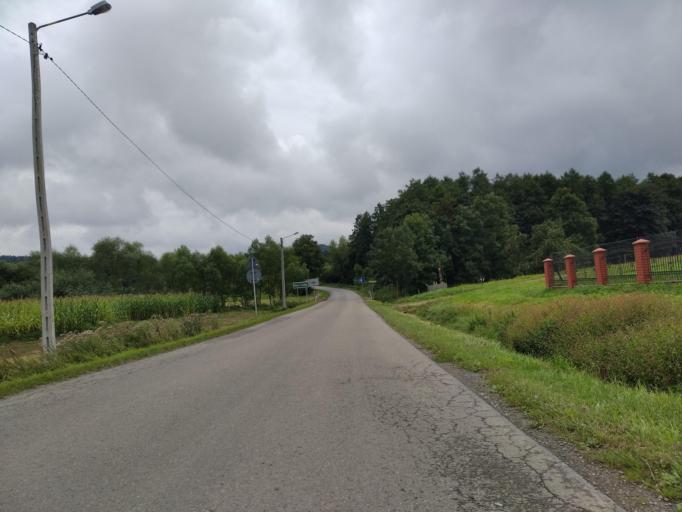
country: PL
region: Subcarpathian Voivodeship
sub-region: Powiat brzozowski
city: Nozdrzec
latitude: 49.7279
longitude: 22.2784
